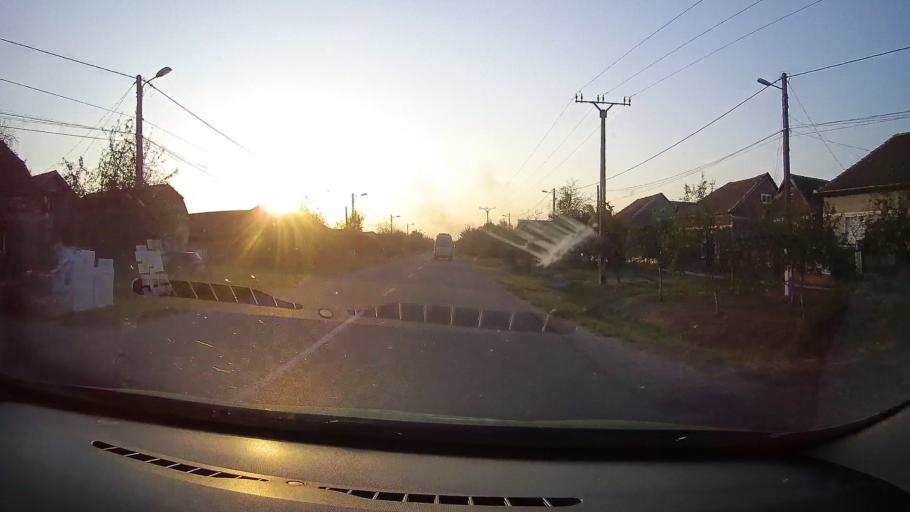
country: RO
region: Arad
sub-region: Comuna Sicula
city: Sicula
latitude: 46.4365
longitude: 21.7685
